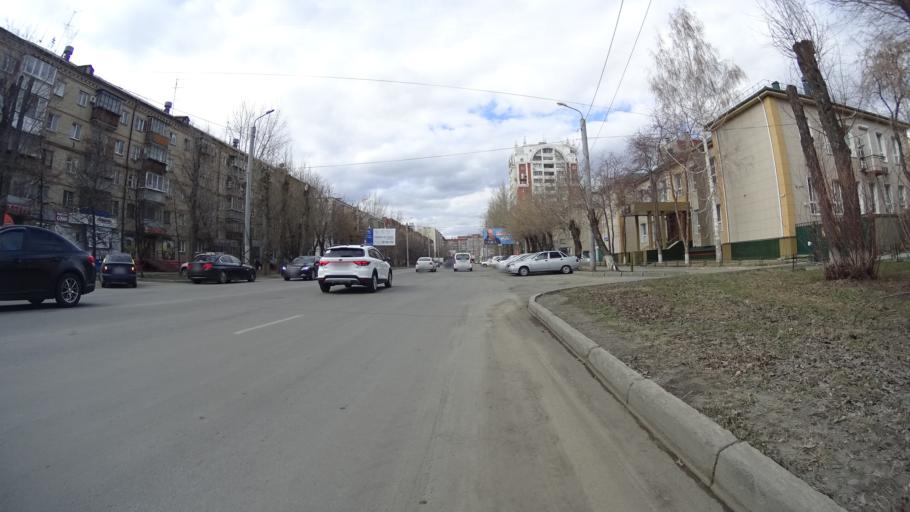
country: RU
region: Chelyabinsk
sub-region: Gorod Chelyabinsk
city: Chelyabinsk
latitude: 55.1493
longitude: 61.3806
